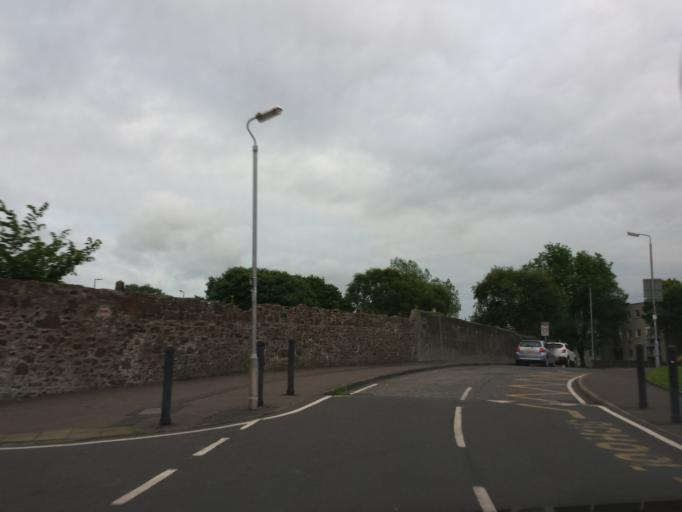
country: GB
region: Scotland
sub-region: South Ayrshire
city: Ayr
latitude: 55.4675
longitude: -4.6230
